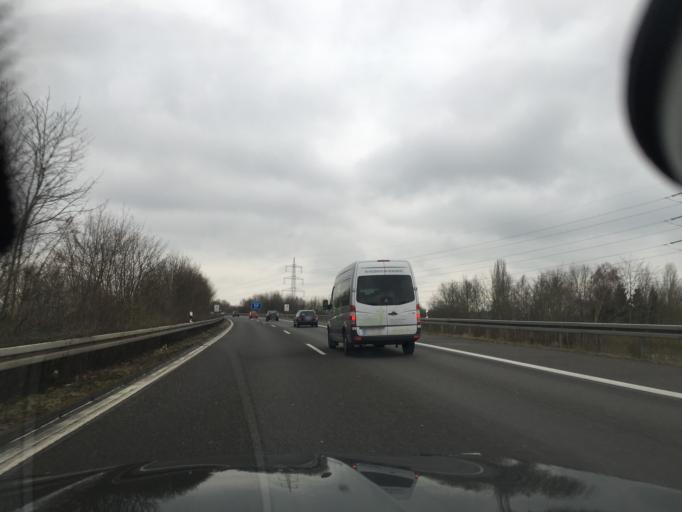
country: DE
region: North Rhine-Westphalia
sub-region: Regierungsbezirk Koln
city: Gremberghoven
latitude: 50.9095
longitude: 7.0666
